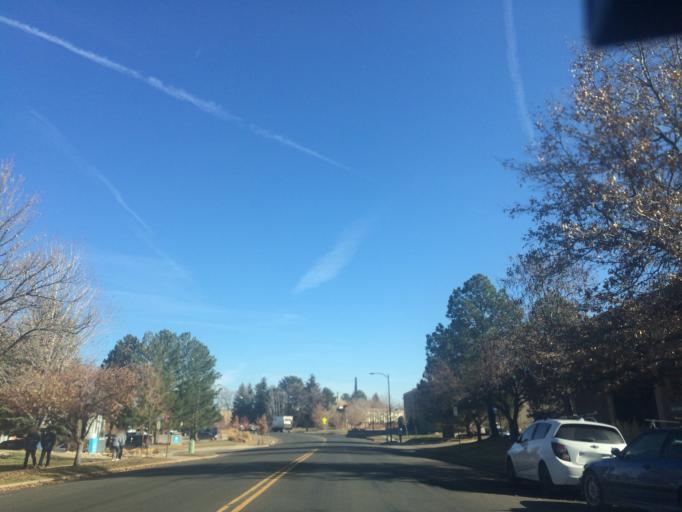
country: US
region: Colorado
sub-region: Boulder County
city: Boulder
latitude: 40.0197
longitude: -105.2216
